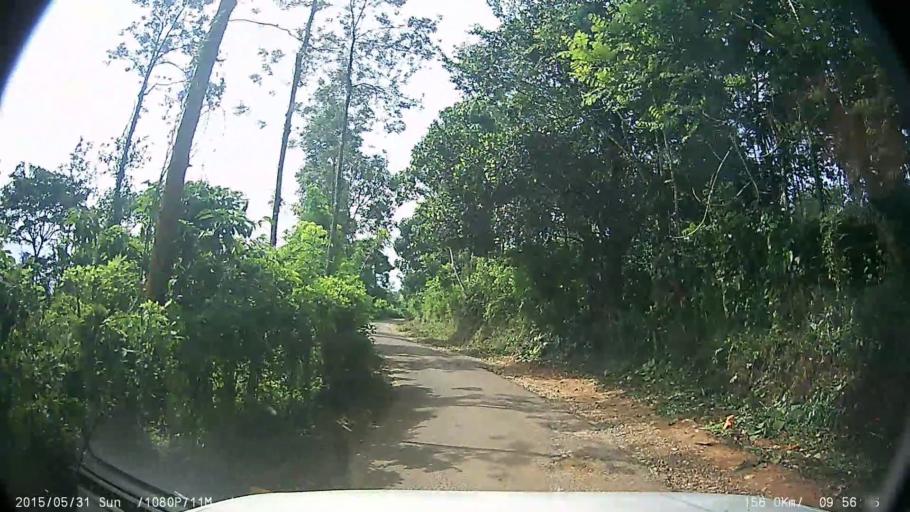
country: IN
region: Kerala
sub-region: Wayanad
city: Kalpetta
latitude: 11.5961
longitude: 76.0577
